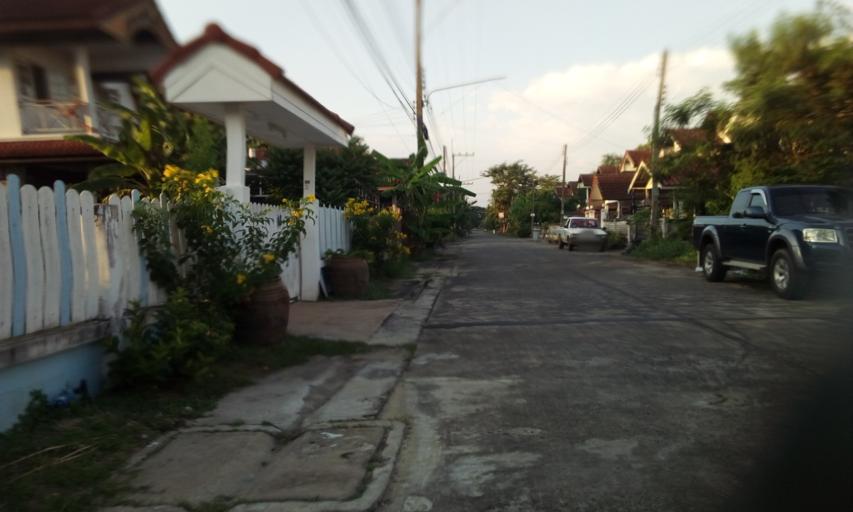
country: TH
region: Pathum Thani
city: Ban Rangsit
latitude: 14.0481
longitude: 100.8224
